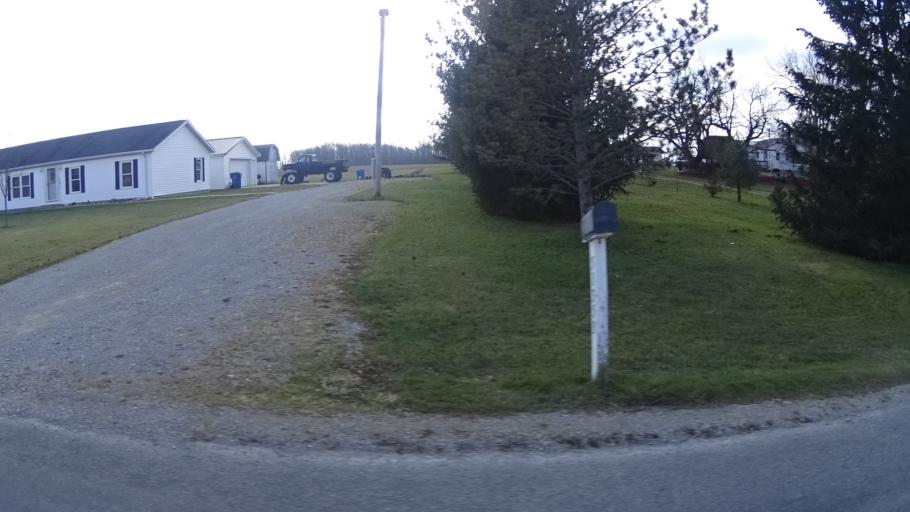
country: US
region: Ohio
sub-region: Lorain County
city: Camden
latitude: 41.2155
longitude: -82.3157
